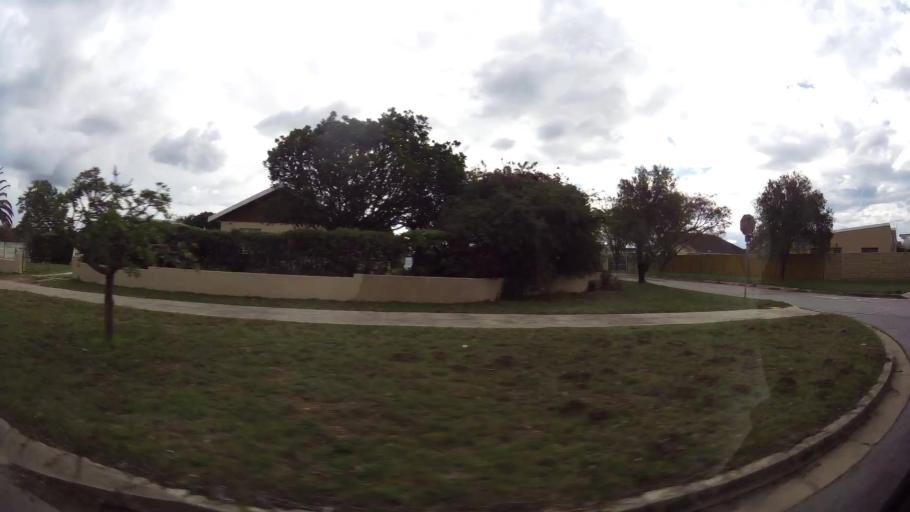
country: ZA
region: Eastern Cape
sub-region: Nelson Mandela Bay Metropolitan Municipality
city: Port Elizabeth
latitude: -33.9391
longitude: 25.5217
